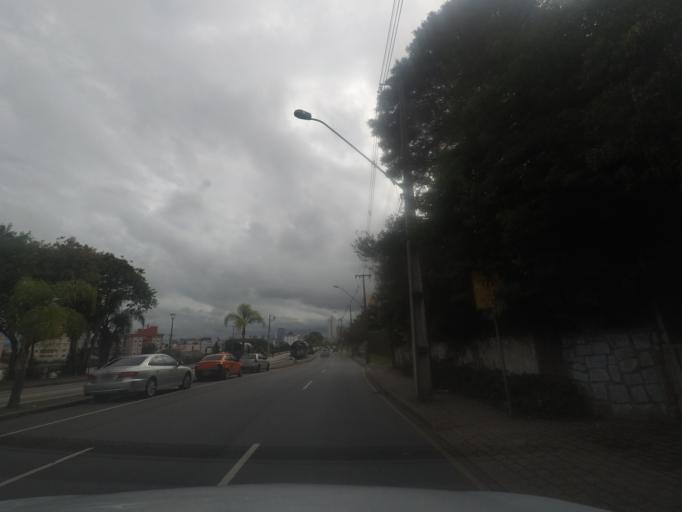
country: BR
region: Parana
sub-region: Curitiba
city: Curitiba
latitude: -25.4371
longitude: -49.2430
